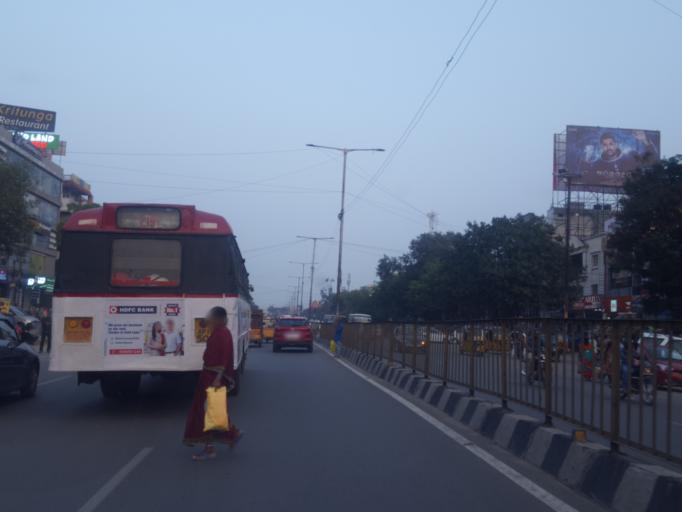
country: IN
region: Telangana
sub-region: Medak
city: Serilingampalle
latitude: 17.4952
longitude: 78.3219
